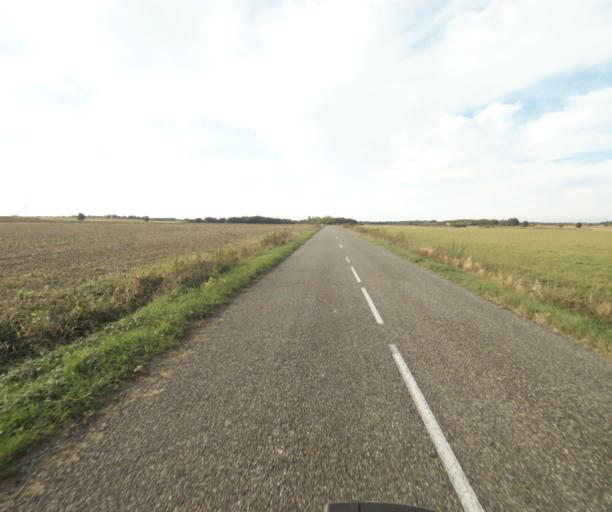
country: FR
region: Midi-Pyrenees
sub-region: Departement du Tarn-et-Garonne
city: Finhan
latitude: 43.9075
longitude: 1.1166
